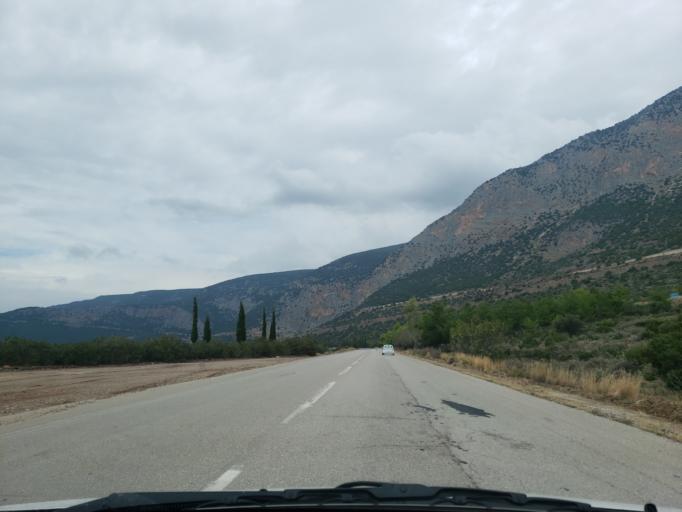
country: GR
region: Central Greece
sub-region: Nomos Fokidos
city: Delphi
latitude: 38.4836
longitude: 22.4611
